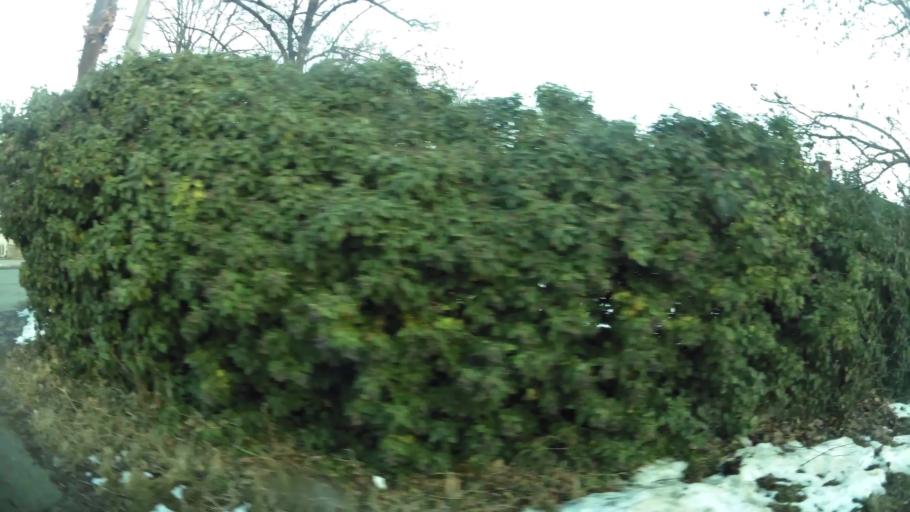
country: MK
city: Creshevo
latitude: 42.0101
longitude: 21.5072
